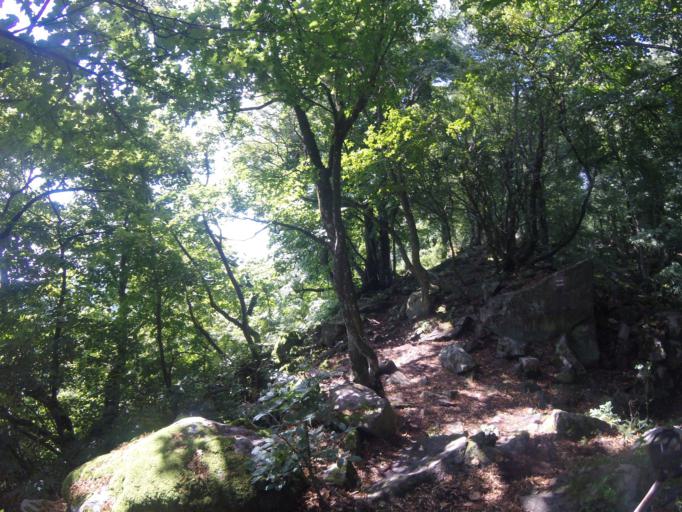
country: SK
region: Nitriansky
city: Sahy
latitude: 47.9798
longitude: 18.8878
